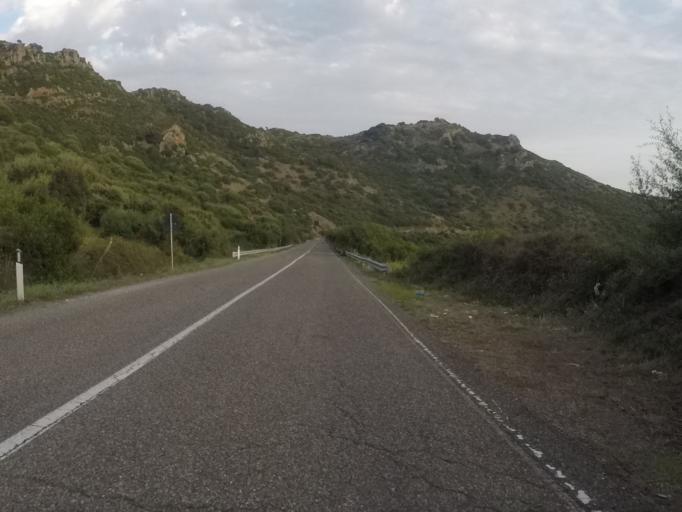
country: IT
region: Sardinia
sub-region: Provincia di Oristano
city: Montresta
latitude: 40.3548
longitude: 8.4249
